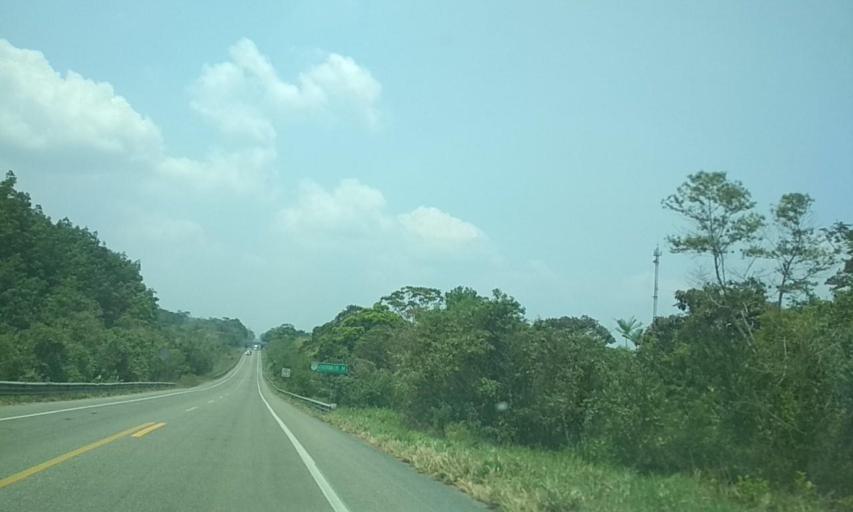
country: MX
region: Tabasco
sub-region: Huimanguillo
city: Francisco Rueda
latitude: 17.6700
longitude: -93.8690
